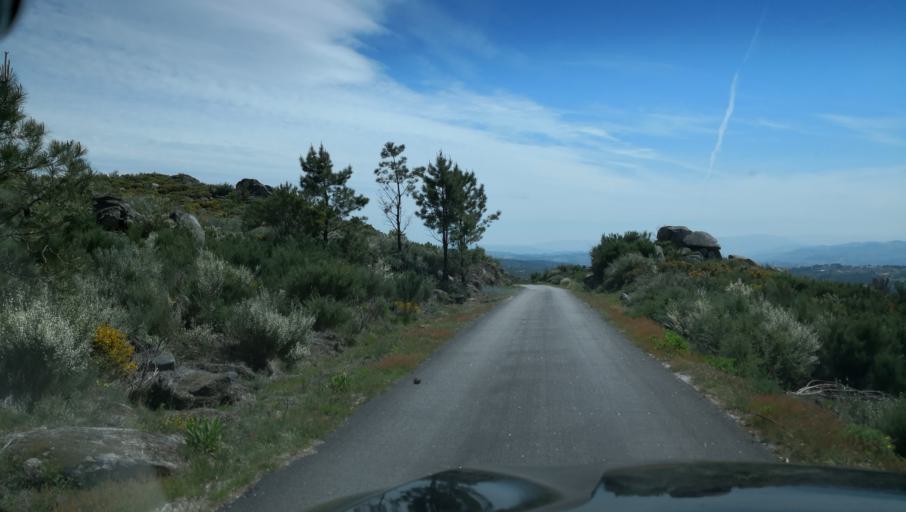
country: PT
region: Vila Real
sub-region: Vila Real
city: Vila Real
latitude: 41.3692
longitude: -7.6996
